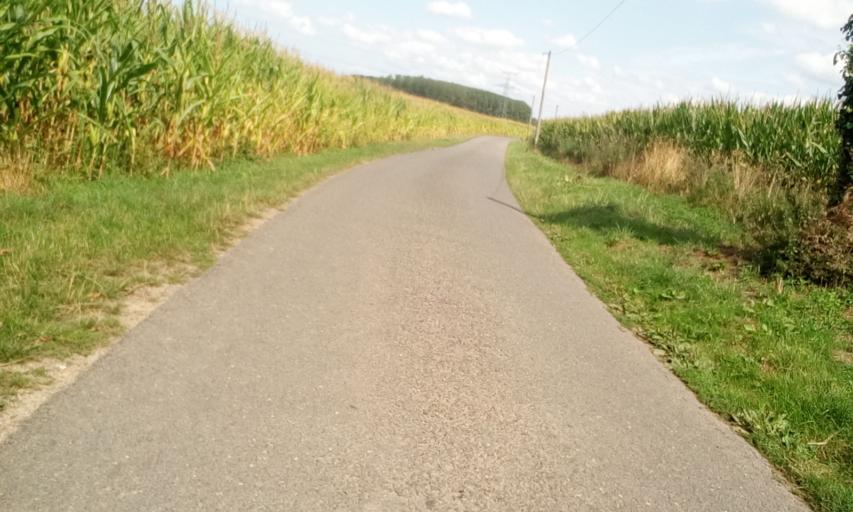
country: FR
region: Lower Normandy
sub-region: Departement du Calvados
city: Bellengreville
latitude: 49.1298
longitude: -0.1935
